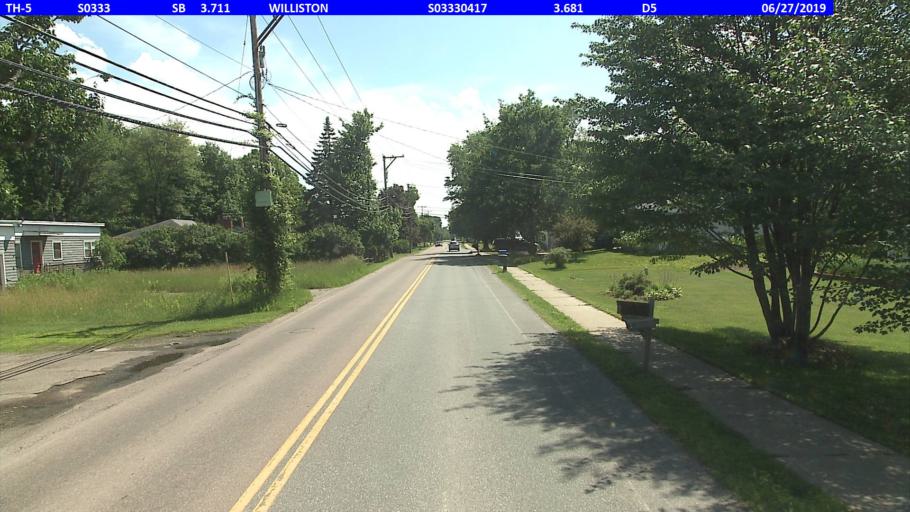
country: US
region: Vermont
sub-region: Chittenden County
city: Essex Junction
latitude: 44.4528
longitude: -73.1244
